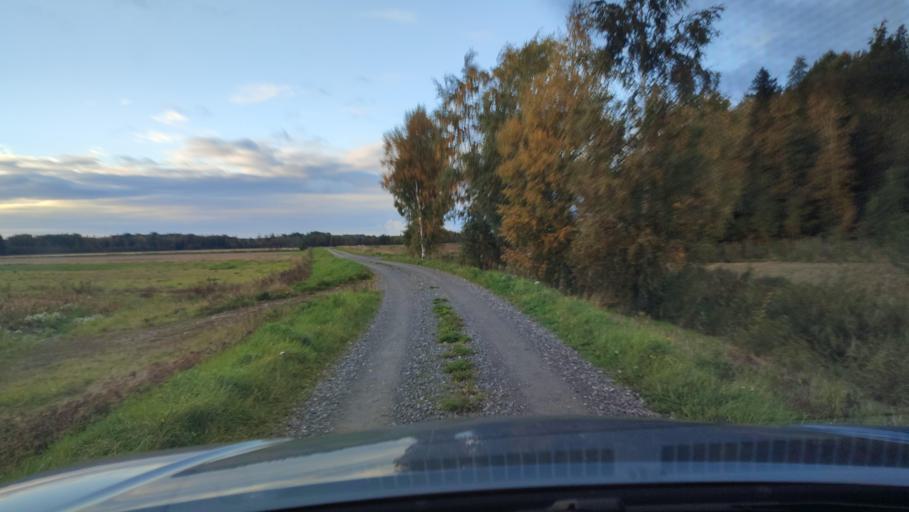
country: FI
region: Ostrobothnia
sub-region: Sydosterbotten
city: Kristinestad
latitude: 62.2444
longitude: 21.4525
